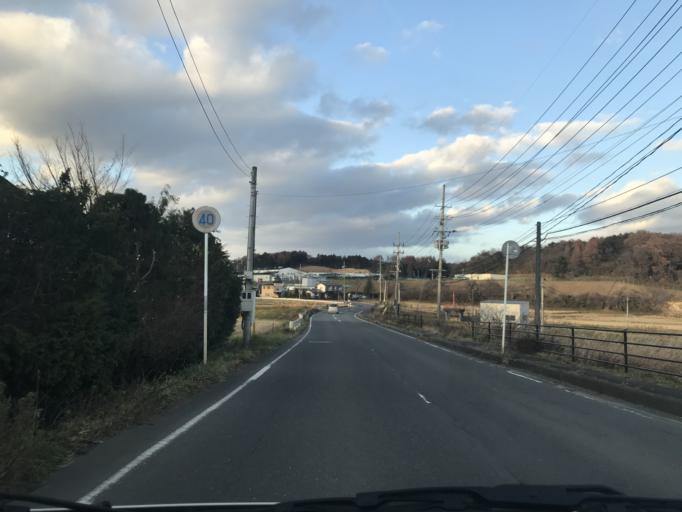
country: JP
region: Miyagi
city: Furukawa
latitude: 38.6639
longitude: 141.0116
